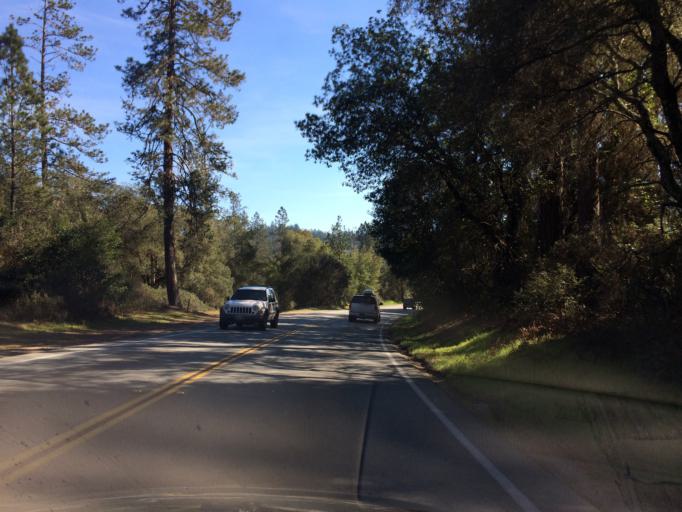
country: US
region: California
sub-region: Santa Cruz County
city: Mount Hermon
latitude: 37.0415
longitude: -122.0461
